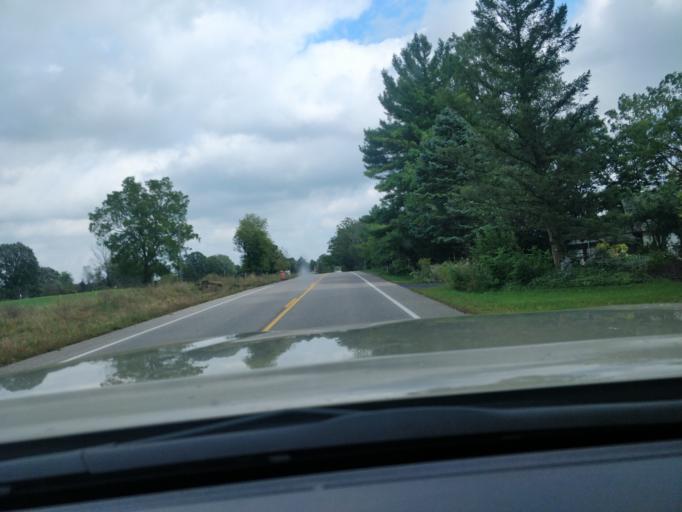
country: US
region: Michigan
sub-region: Kent County
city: Lowell
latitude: 42.8859
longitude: -85.3242
